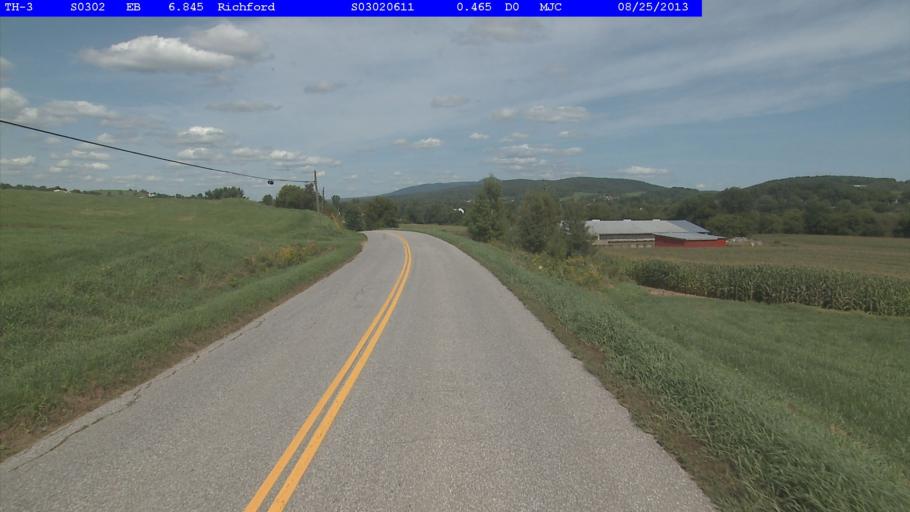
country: US
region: Vermont
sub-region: Franklin County
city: Richford
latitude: 44.9929
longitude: -72.6869
